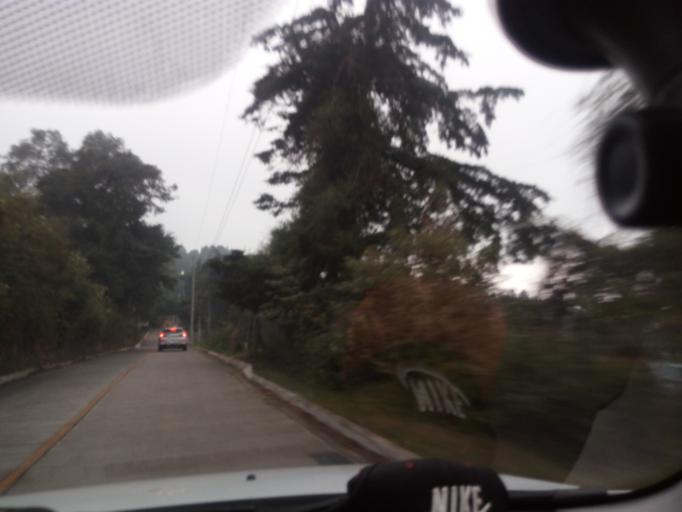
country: GT
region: Sacatepequez
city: Santa Lucia Milpas Altas
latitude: 14.5845
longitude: -90.7103
